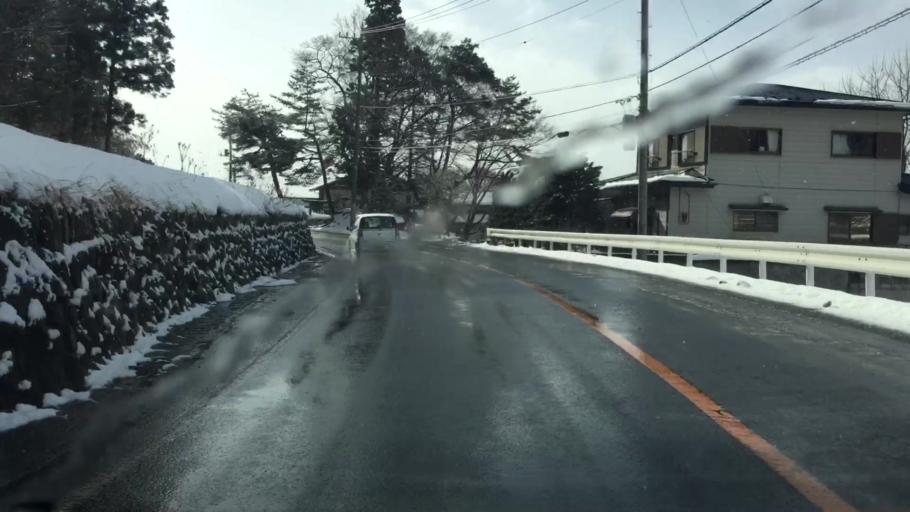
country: JP
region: Gunma
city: Numata
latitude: 36.6736
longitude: 139.0628
